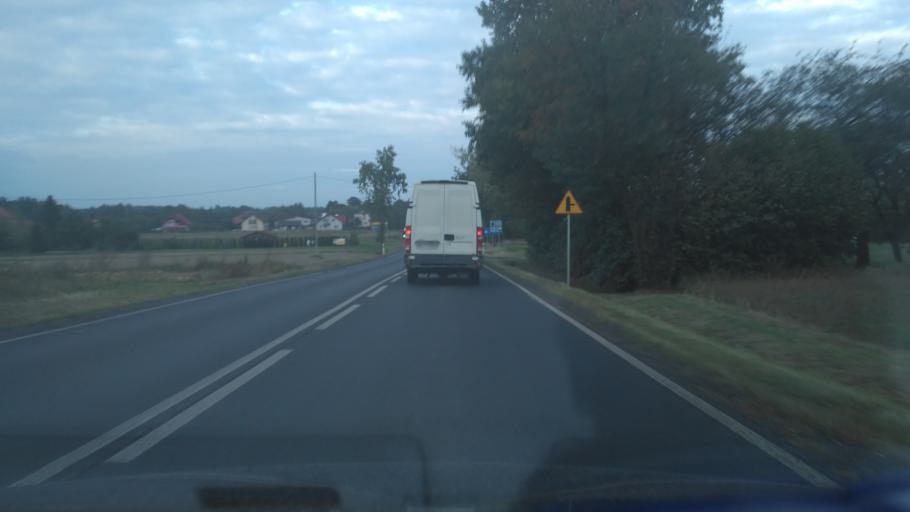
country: PL
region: Lublin Voivodeship
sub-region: Powiat leczynski
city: Spiczyn
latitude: 51.2968
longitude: 22.7166
